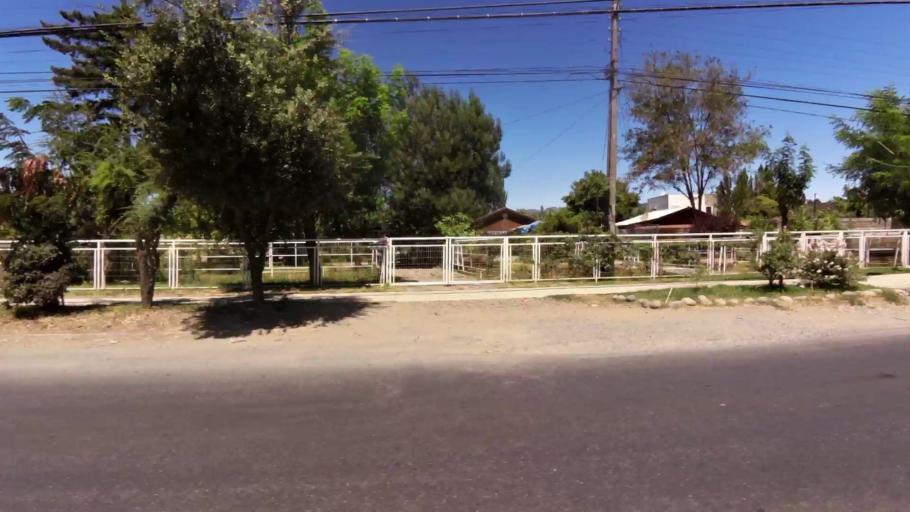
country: CL
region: O'Higgins
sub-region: Provincia de Cachapoal
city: Rancagua
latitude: -34.1669
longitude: -70.7729
